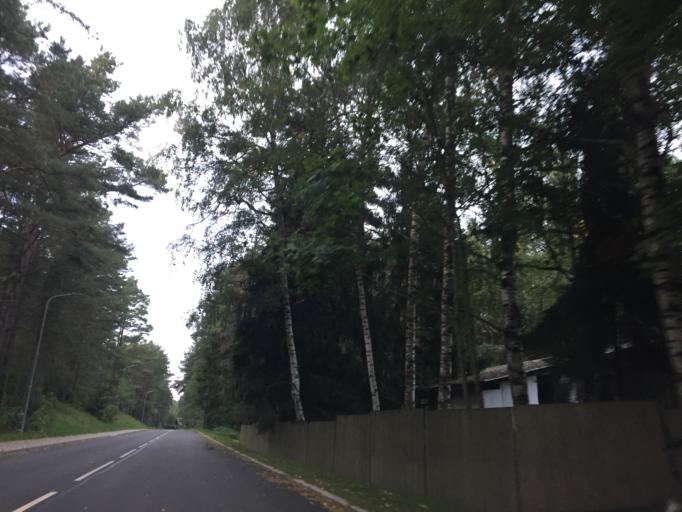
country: LV
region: Saulkrastu
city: Saulkrasti
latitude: 57.3209
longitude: 24.4109
